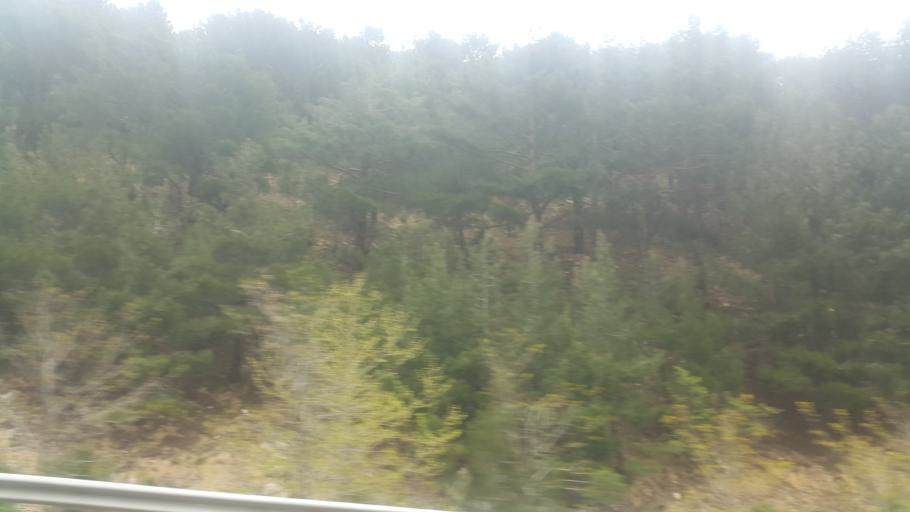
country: TR
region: Adana
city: Pozanti
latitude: 37.4889
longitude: 34.8454
